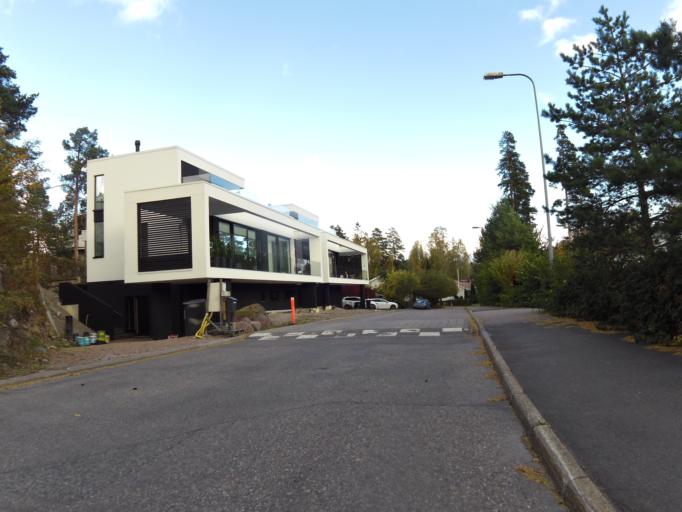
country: FI
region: Uusimaa
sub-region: Helsinki
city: Koukkuniemi
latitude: 60.1459
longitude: 24.7372
